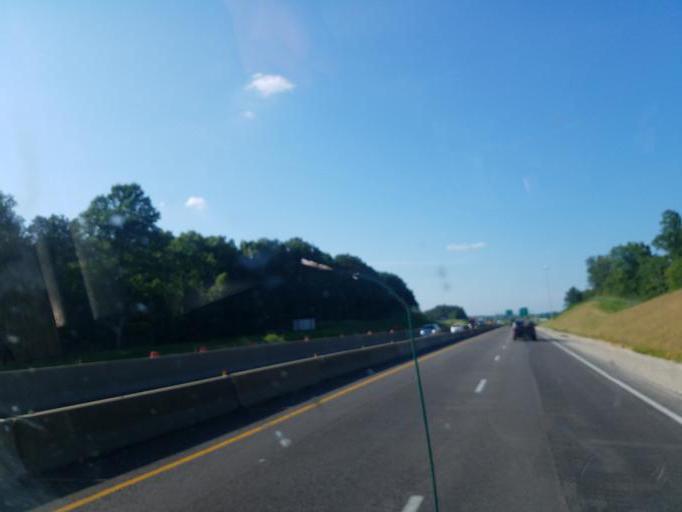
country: US
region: Kentucky
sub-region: Hardin County
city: Elizabethtown
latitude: 37.6624
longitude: -85.8542
